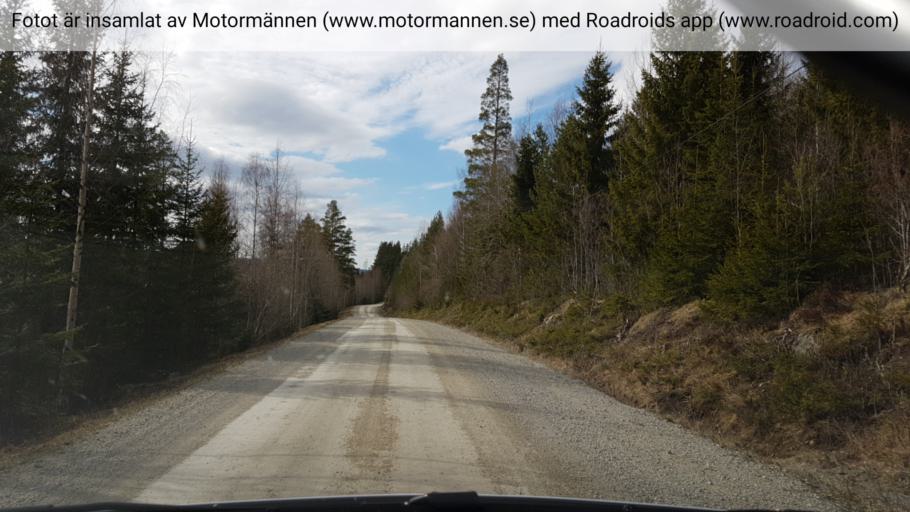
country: SE
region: Jaemtland
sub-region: Bergs Kommun
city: Hoverberg
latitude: 62.6926
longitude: 14.7267
